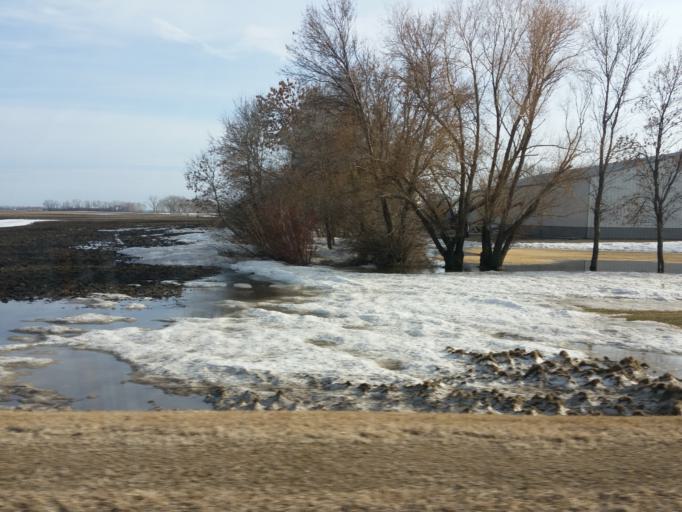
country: US
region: North Dakota
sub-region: Walsh County
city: Grafton
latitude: 48.4265
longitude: -97.2252
